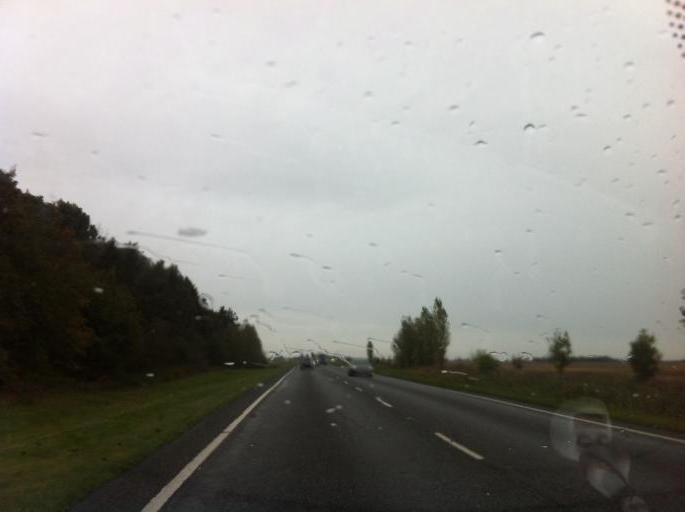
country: GB
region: England
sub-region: Lincolnshire
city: Crowland
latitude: 52.6965
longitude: -0.1295
